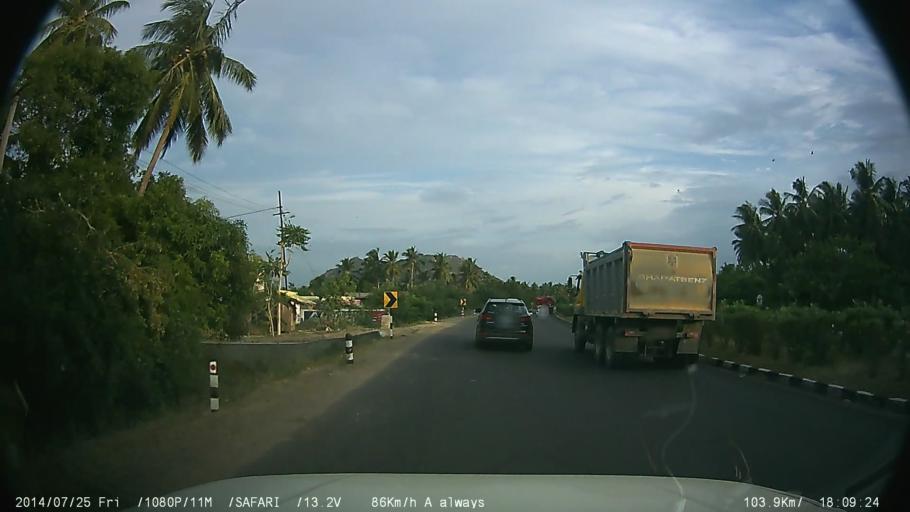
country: IN
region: Tamil Nadu
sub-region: Krishnagiri
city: Kaverippattanam
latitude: 12.3892
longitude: 78.2194
